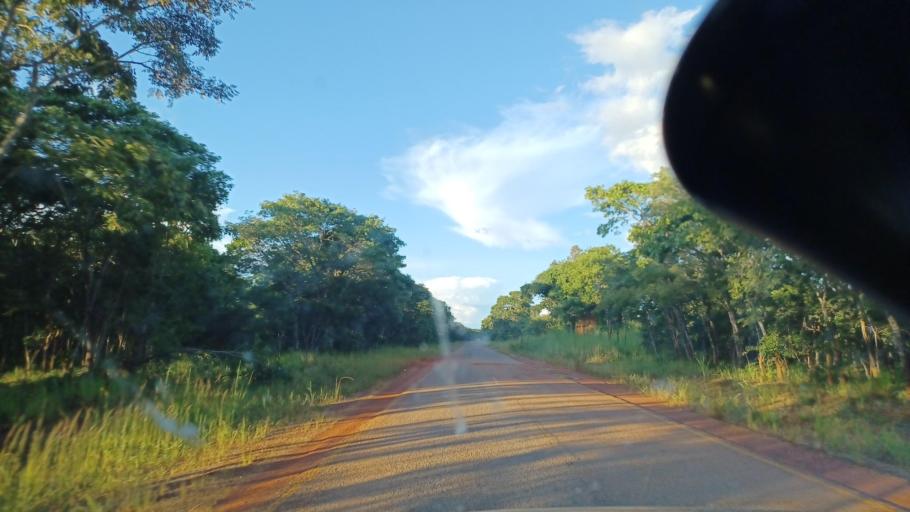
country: ZM
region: North-Western
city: Kalengwa
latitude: -13.1114
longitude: 25.2179
